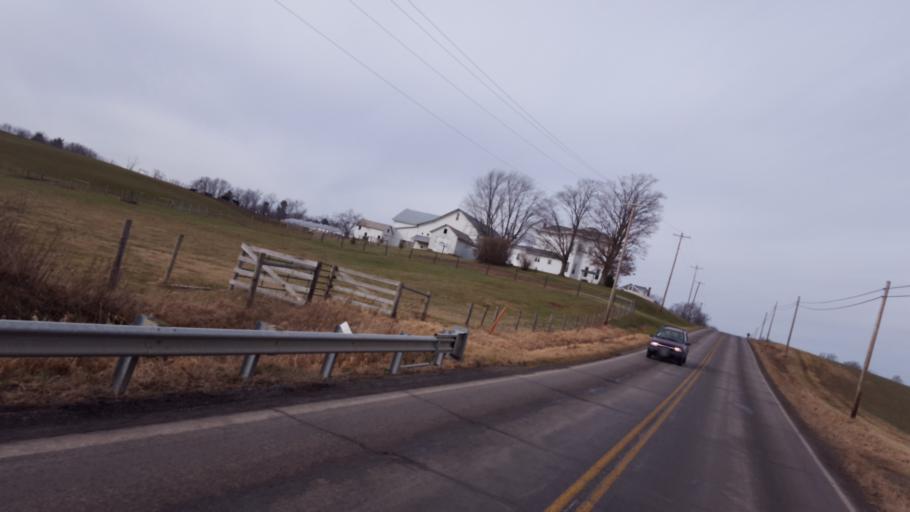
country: US
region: Ohio
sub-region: Wayne County
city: Apple Creek
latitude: 40.6935
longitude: -81.8809
